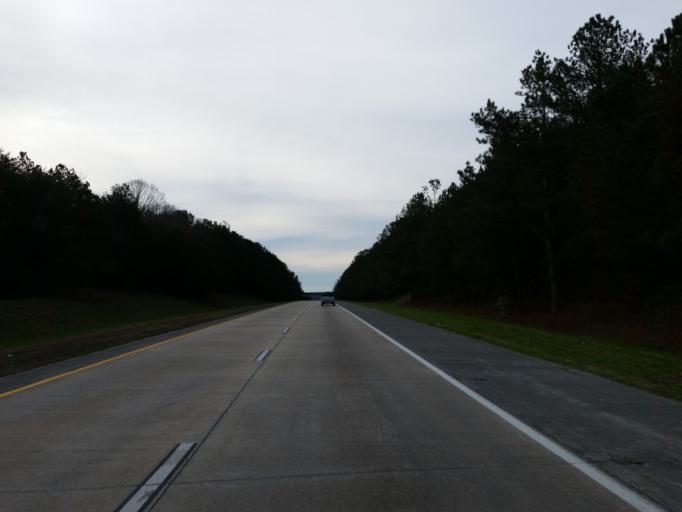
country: US
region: Georgia
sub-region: Pickens County
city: Nelson
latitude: 34.3648
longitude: -84.3917
